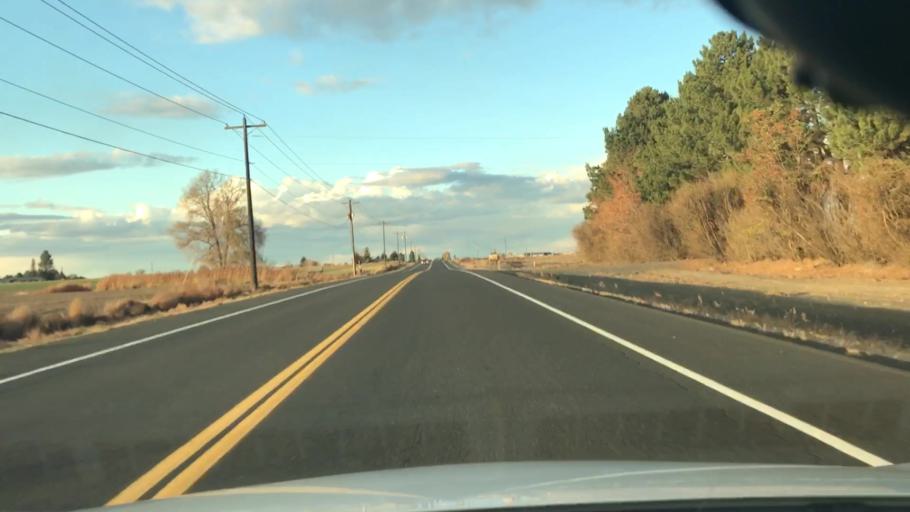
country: US
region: Washington
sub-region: Grant County
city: Moses Lake
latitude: 47.1106
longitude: -119.2360
